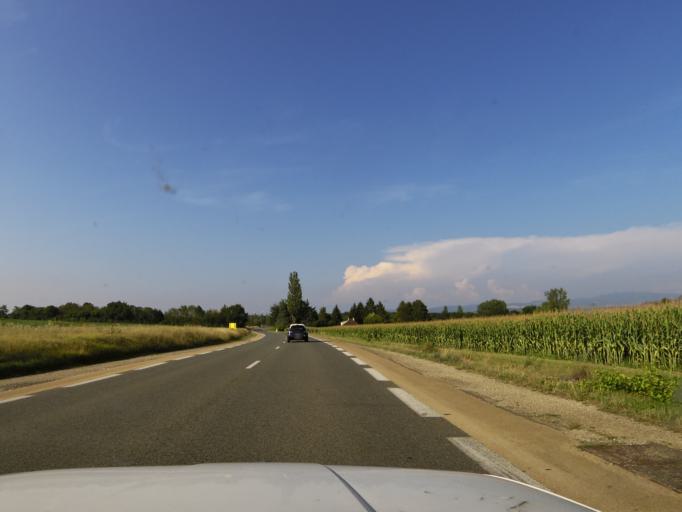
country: FR
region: Rhone-Alpes
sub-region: Departement de l'Isere
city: Hieres-sur-Amby
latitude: 45.8183
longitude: 5.2805
